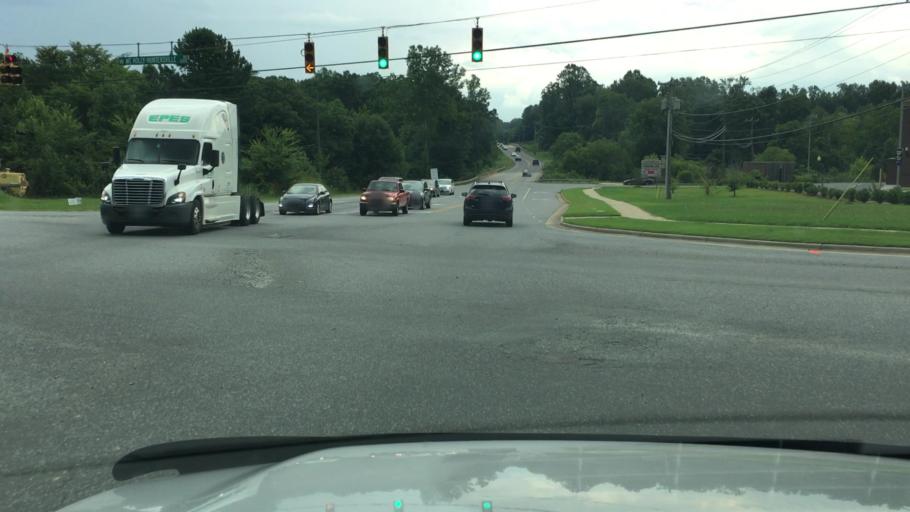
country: US
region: North Carolina
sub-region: Mecklenburg County
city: Huntersville
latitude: 35.3465
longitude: -80.8855
